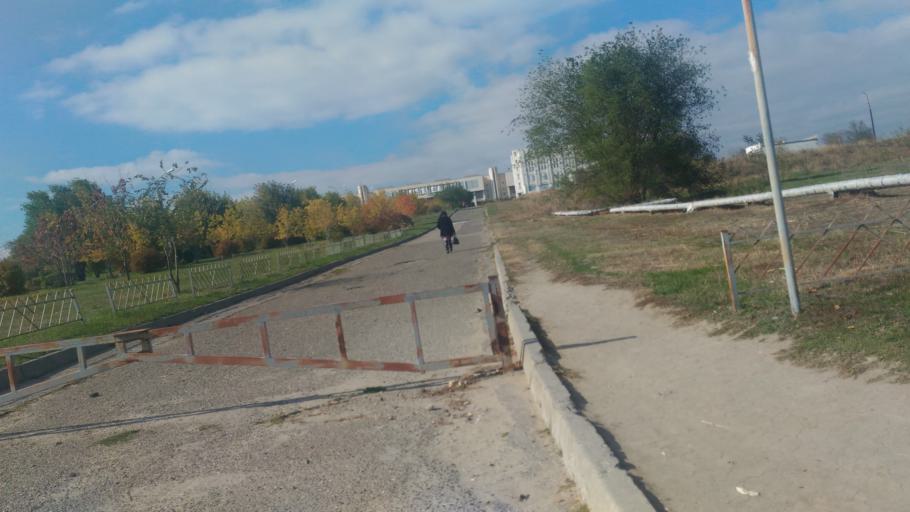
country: RU
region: Volgograd
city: Volgograd
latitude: 48.6411
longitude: 44.4294
